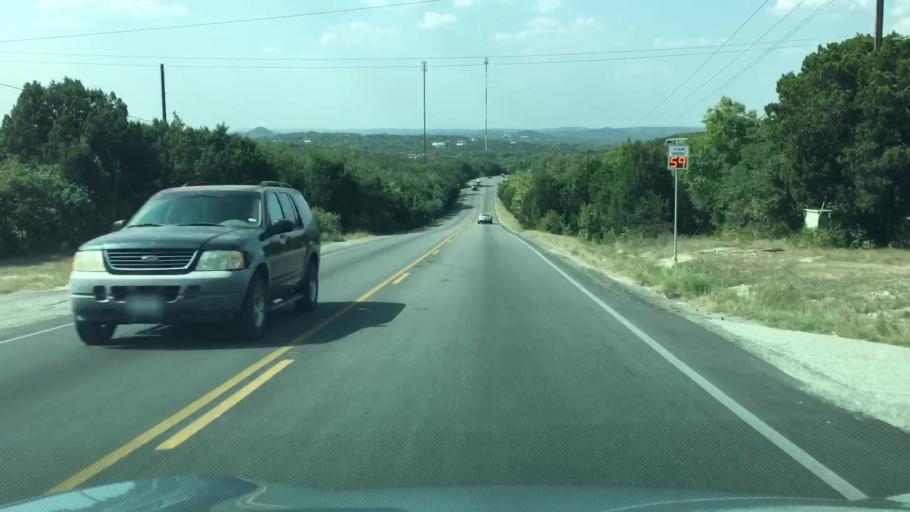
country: US
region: Texas
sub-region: Hays County
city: Wimberley
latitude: 29.9664
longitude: -98.0918
